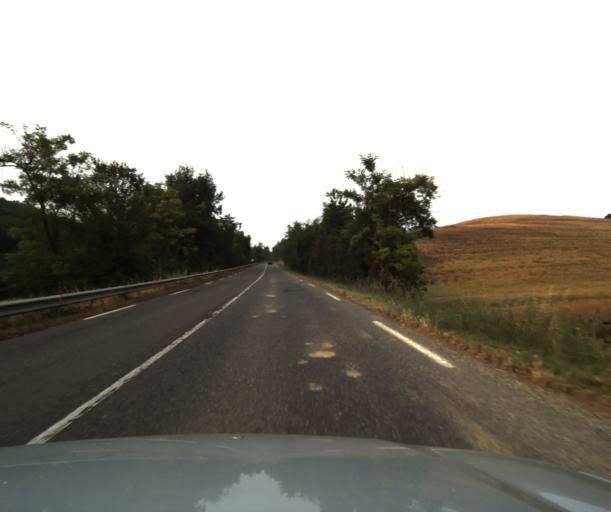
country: FR
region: Midi-Pyrenees
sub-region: Departement du Gers
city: Mirande
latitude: 43.5568
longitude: 0.4965
